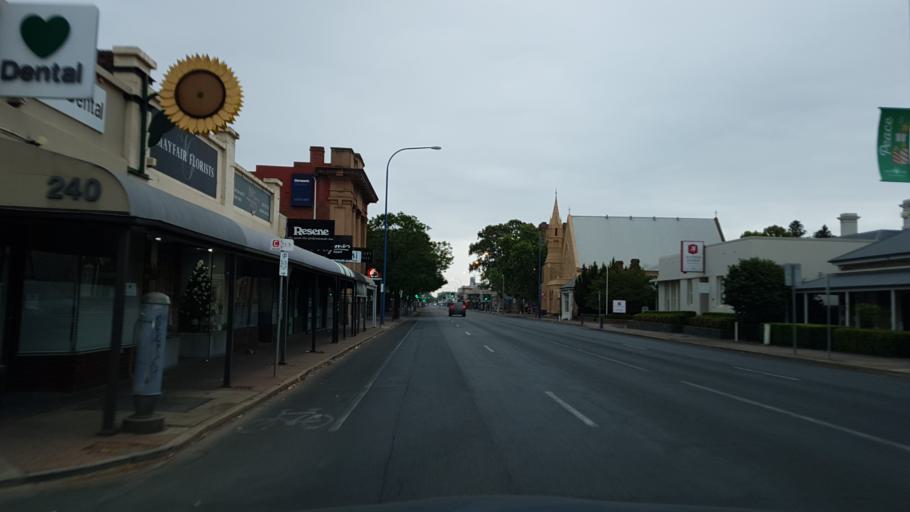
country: AU
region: South Australia
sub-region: Unley
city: Unley
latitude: -34.9527
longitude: 138.6075
